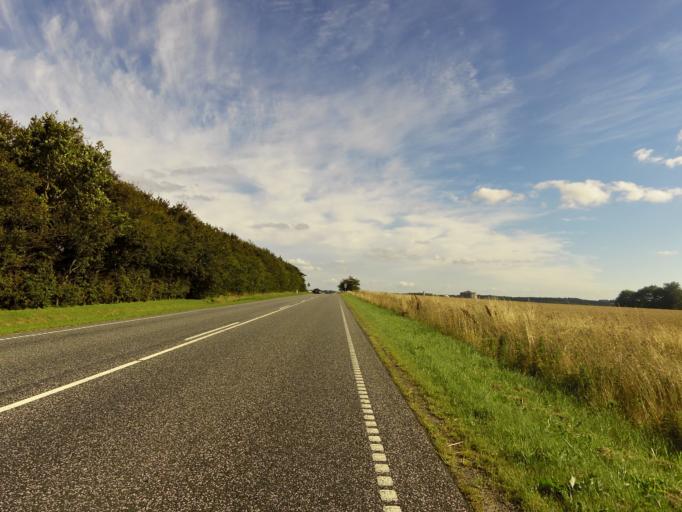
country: DK
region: South Denmark
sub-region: Tonder Kommune
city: Toftlund
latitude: 55.1849
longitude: 9.0589
